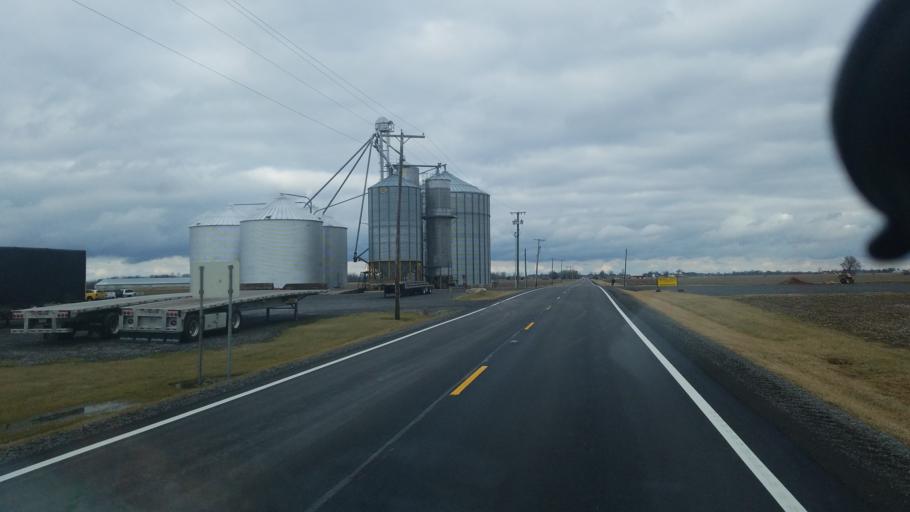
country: US
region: Ohio
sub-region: Marion County
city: Marion
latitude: 40.5859
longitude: -83.0390
